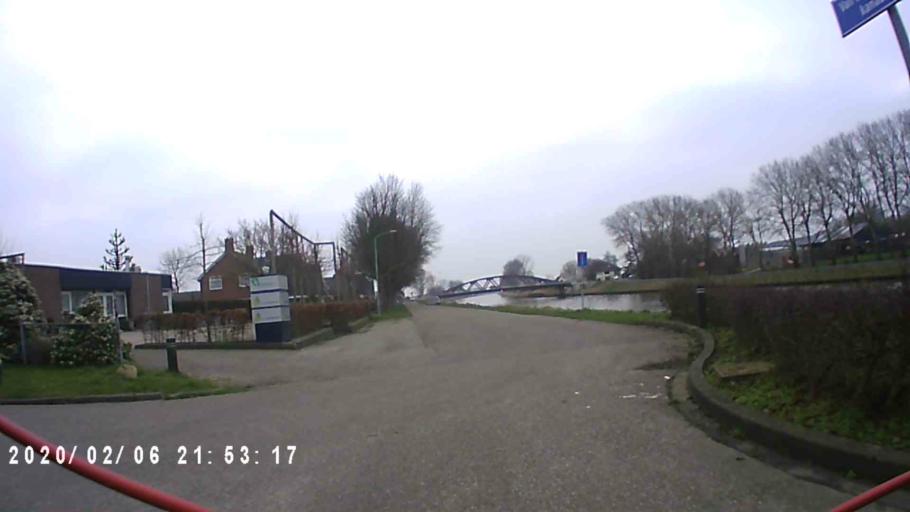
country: NL
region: Groningen
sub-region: Gemeente Zuidhorn
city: Noordhorn
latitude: 53.2546
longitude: 6.3968
